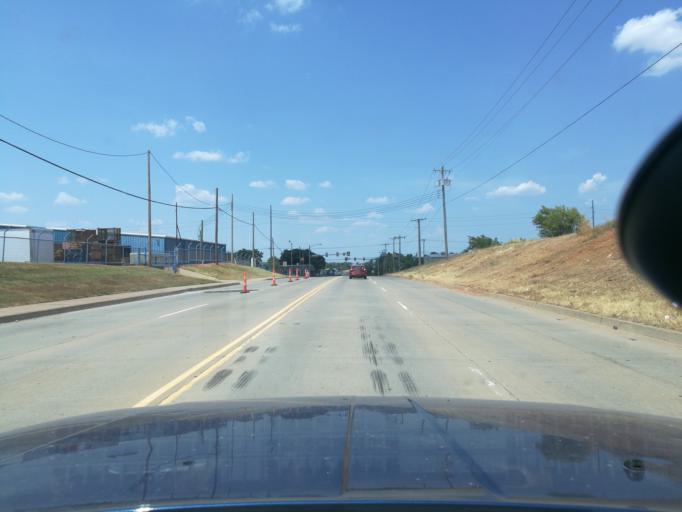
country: US
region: Oklahoma
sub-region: Oklahoma County
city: Del City
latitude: 35.4191
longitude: -97.4770
